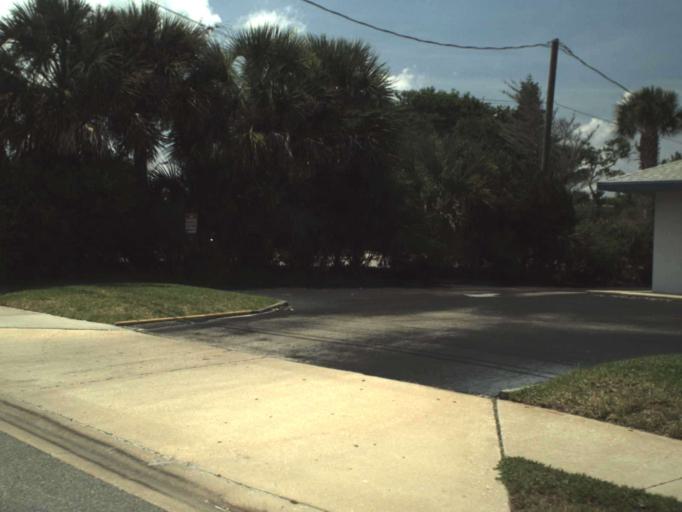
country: US
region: Florida
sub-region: Volusia County
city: New Smyrna Beach
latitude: 29.0289
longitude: -80.8959
